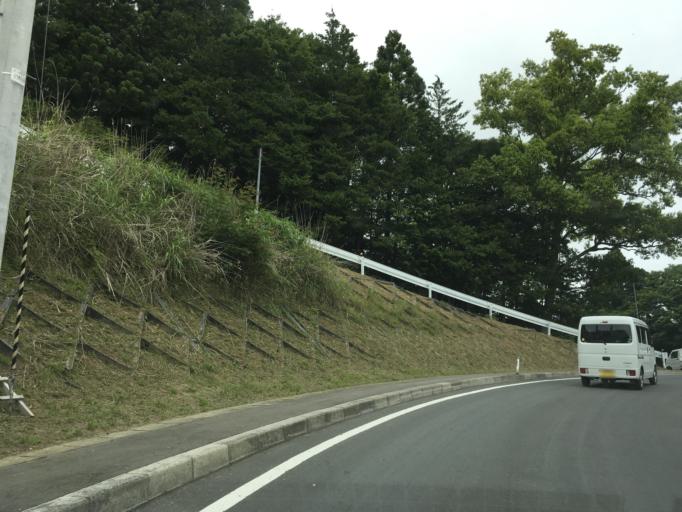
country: JP
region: Iwate
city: Ofunato
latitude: 38.8905
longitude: 141.6382
